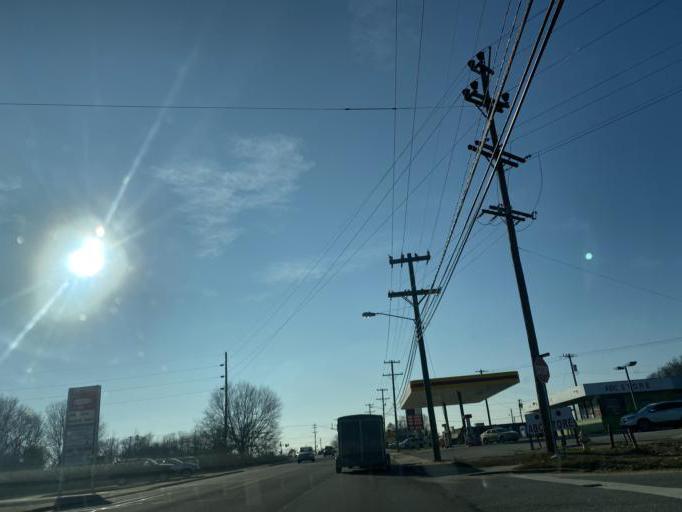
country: US
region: South Carolina
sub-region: Cherokee County
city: Gaffney
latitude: 35.0659
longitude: -81.6609
